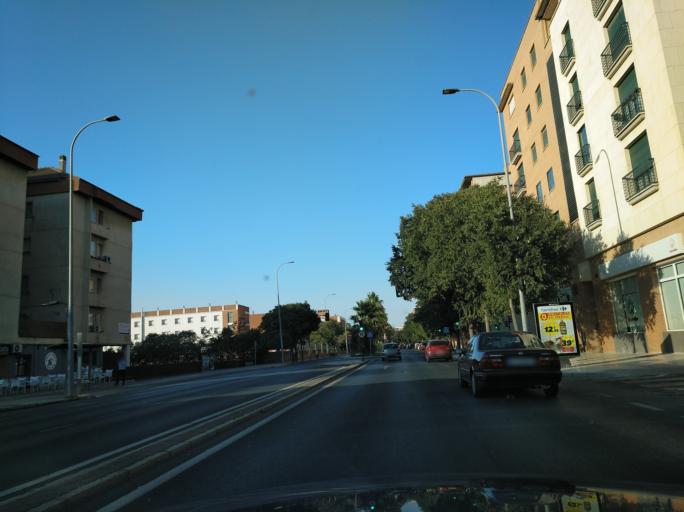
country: ES
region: Extremadura
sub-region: Provincia de Badajoz
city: Badajoz
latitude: 38.8671
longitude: -6.9812
